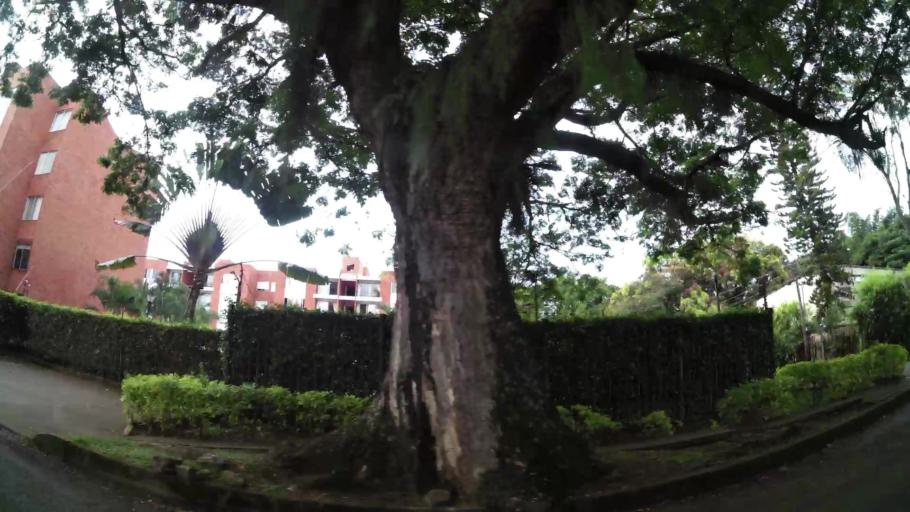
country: CO
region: Valle del Cauca
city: Cali
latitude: 3.3976
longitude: -76.5541
